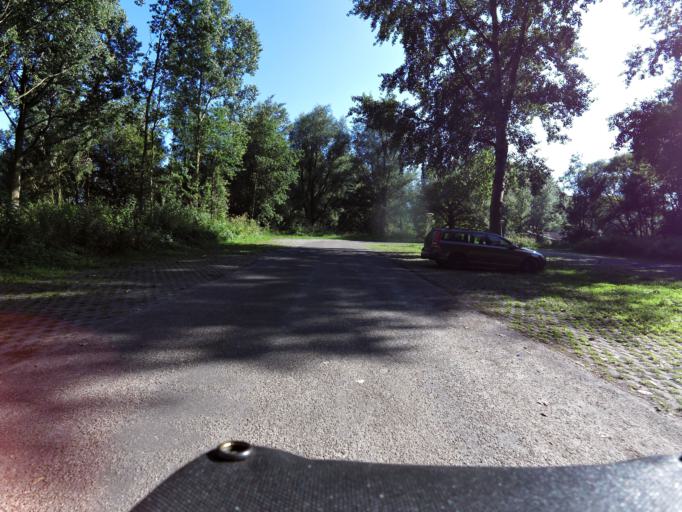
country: NL
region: South Holland
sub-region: Gemeente Dordrecht
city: Dordrecht
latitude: 51.7615
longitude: 4.6934
